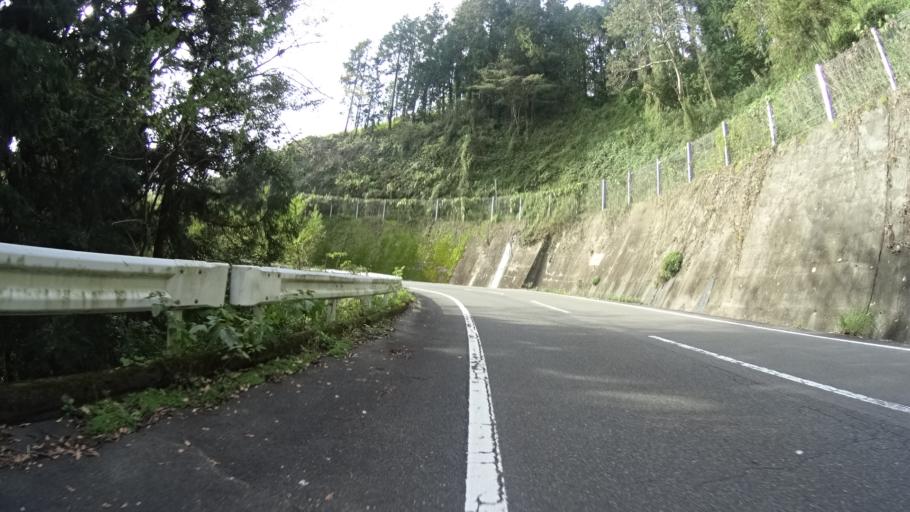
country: JP
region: Yamanashi
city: Uenohara
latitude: 35.6302
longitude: 139.0422
